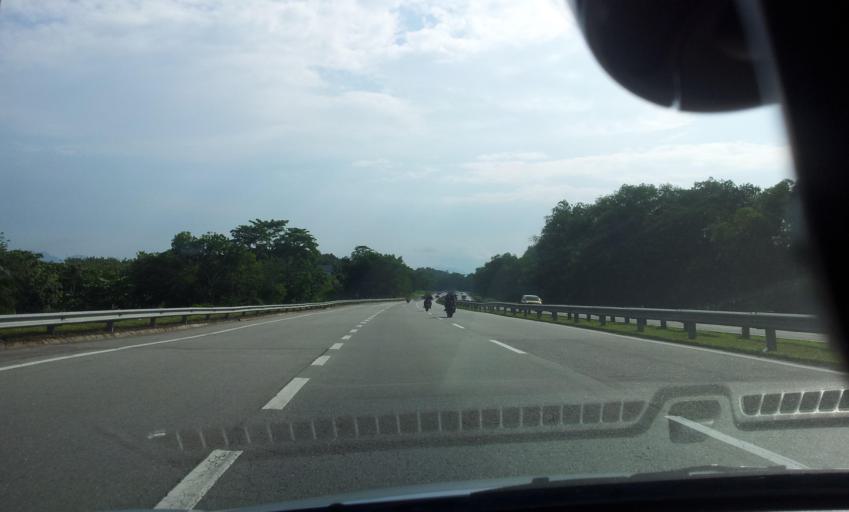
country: MY
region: Pahang
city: Bentong Town
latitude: 3.4929
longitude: 102.0981
